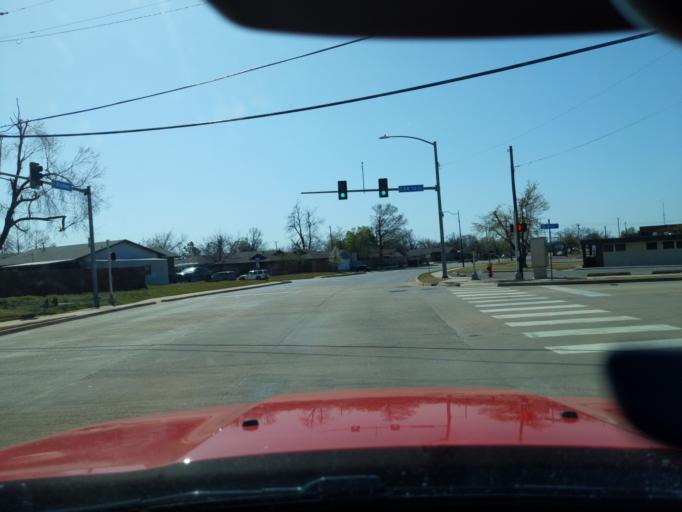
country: US
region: Oklahoma
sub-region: Cleveland County
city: Moore
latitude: 35.3436
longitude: -97.4871
